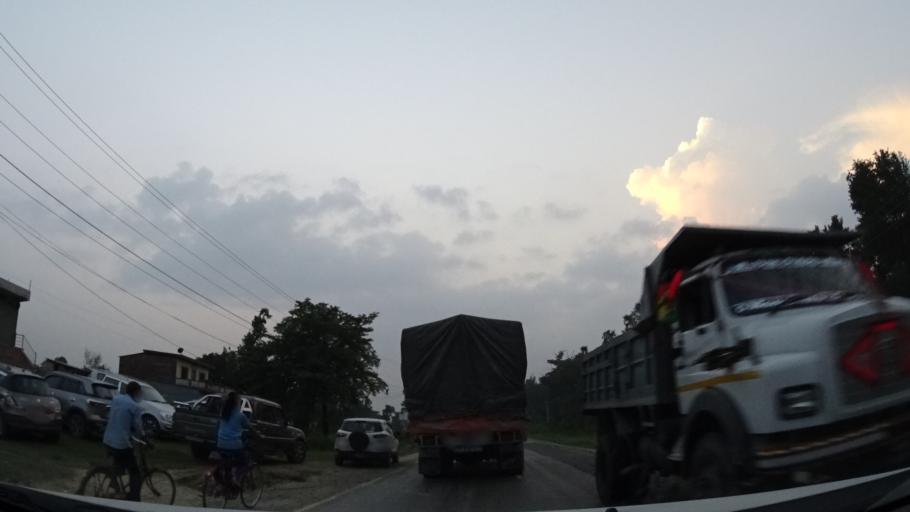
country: IN
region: Uttar Pradesh
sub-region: Maharajganj
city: Nichlaul
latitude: 27.5599
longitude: 83.7705
